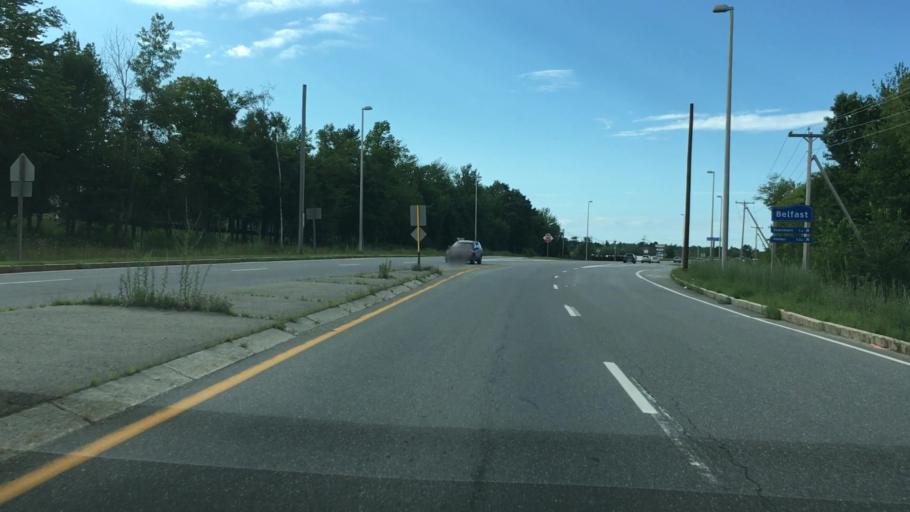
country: US
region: Maine
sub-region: Waldo County
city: Belfast
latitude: 44.4188
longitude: -69.0196
